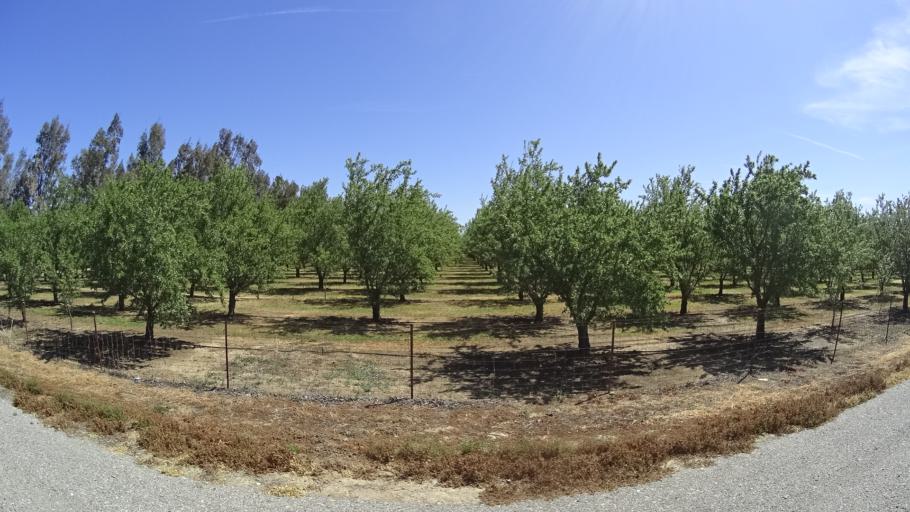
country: US
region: California
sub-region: Glenn County
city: Orland
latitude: 39.7015
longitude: -122.1781
